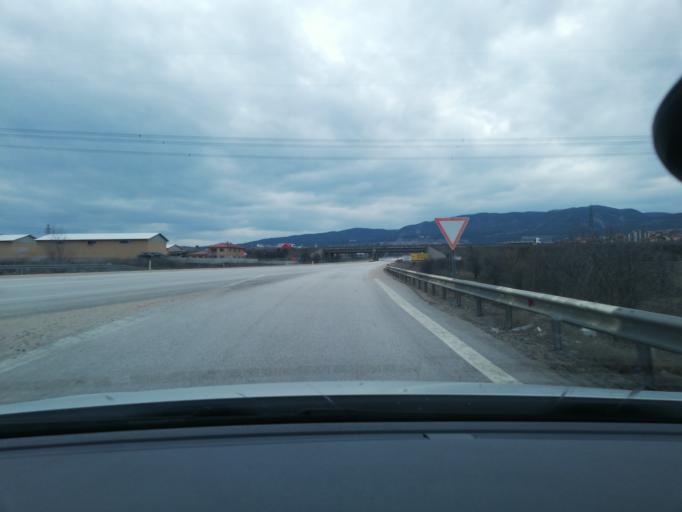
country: TR
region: Bolu
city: Gerede
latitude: 40.7788
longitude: 32.2166
